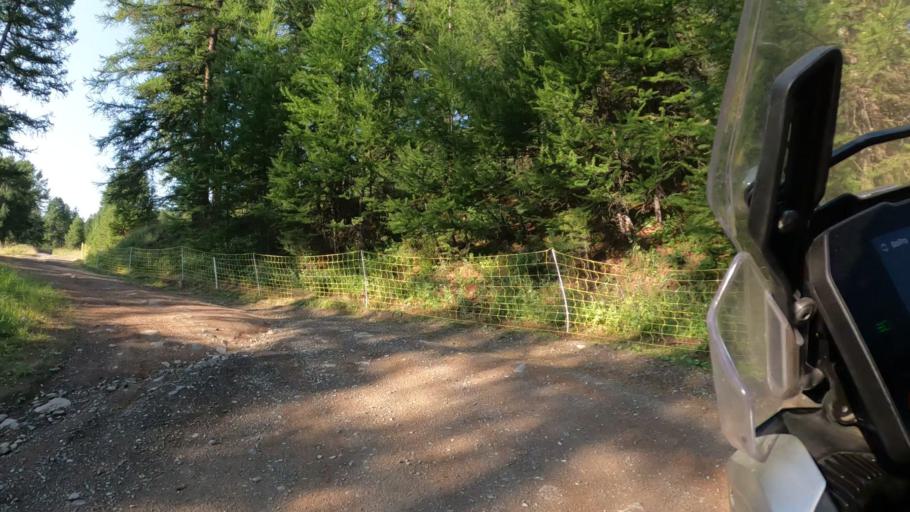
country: FR
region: Provence-Alpes-Cote d'Azur
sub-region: Departement des Hautes-Alpes
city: Guillestre
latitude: 44.6094
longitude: 6.6693
